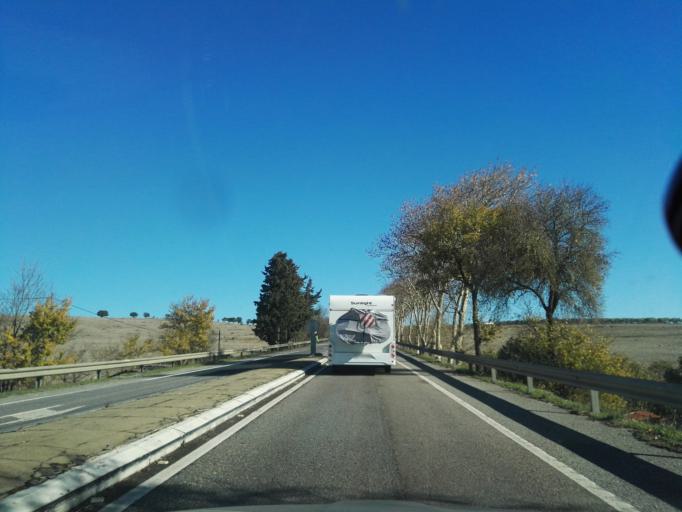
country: PT
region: Evora
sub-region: Vila Vicosa
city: Vila Vicosa
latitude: 38.8488
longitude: -7.3447
